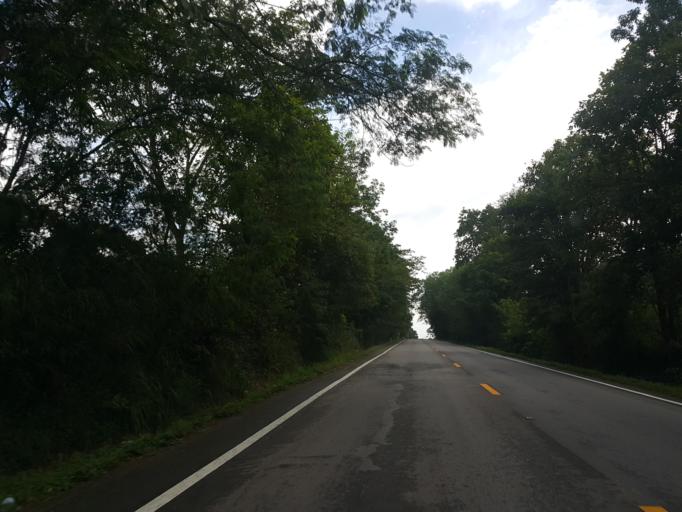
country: TH
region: Chiang Mai
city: Phrao
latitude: 19.2668
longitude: 99.1879
